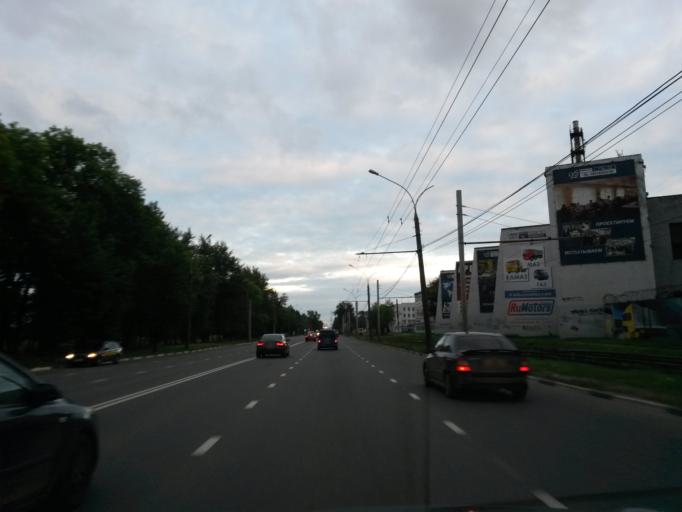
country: RU
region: Jaroslavl
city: Yaroslavl
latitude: 57.6509
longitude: 39.8472
